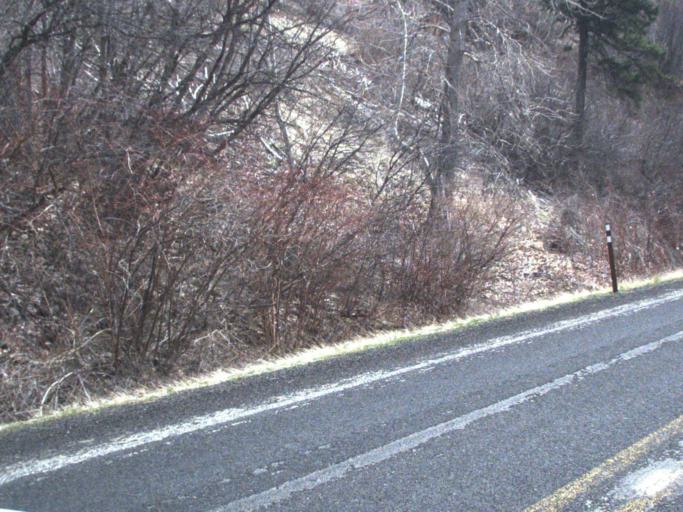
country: US
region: Washington
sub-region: Yakima County
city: Tieton
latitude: 46.8593
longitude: -120.9529
